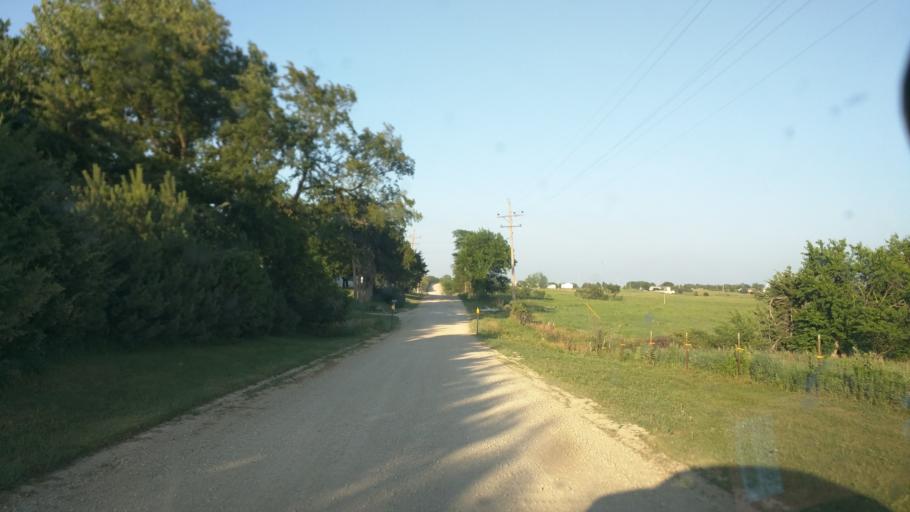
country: US
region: Kansas
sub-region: Riley County
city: Manhattan
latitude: 39.2616
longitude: -96.6917
